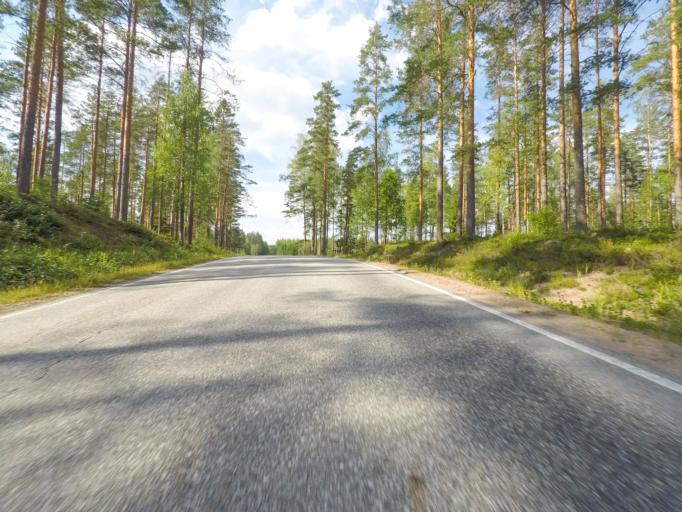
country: FI
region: Southern Savonia
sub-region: Mikkeli
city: Puumala
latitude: 61.6958
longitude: 28.2157
